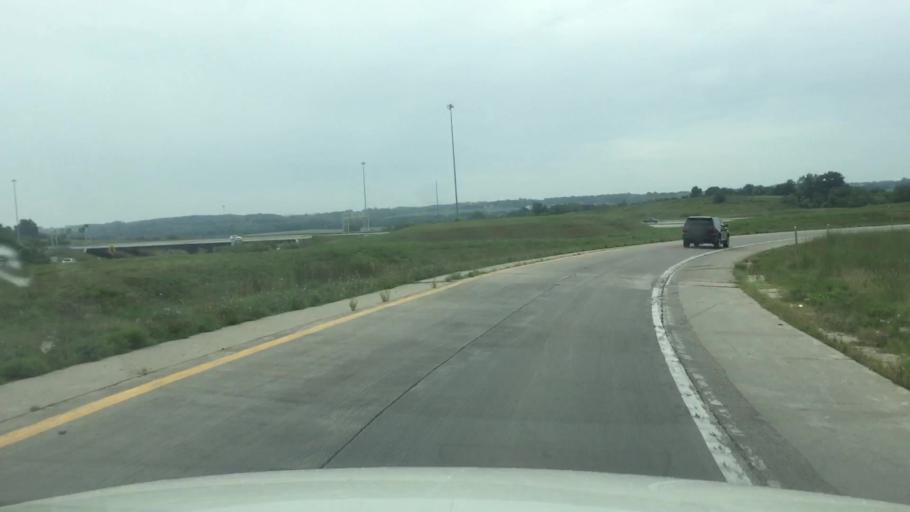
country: US
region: Iowa
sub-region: Warren County
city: Carlisle
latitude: 41.5088
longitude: -93.5747
